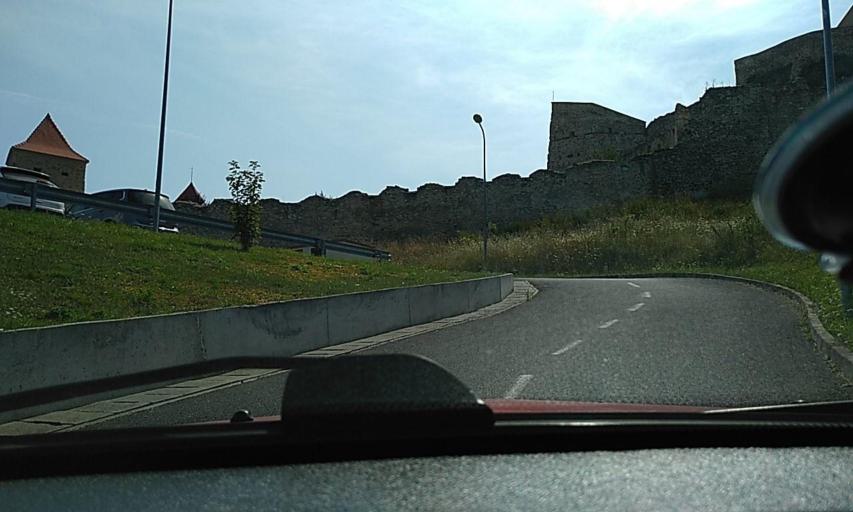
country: RO
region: Brasov
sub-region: Oras Rupea
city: Rupea
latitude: 46.0380
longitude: 25.2113
